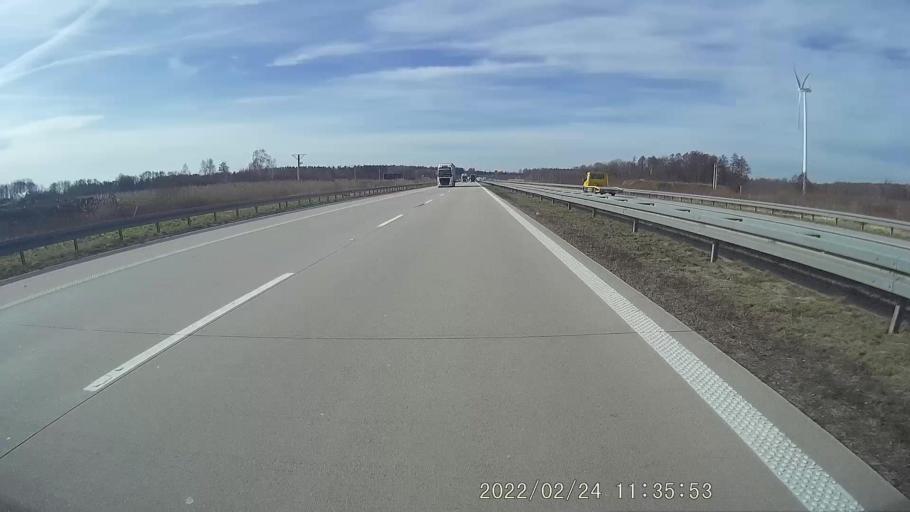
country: PL
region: Lower Silesian Voivodeship
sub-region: Powiat polkowicki
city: Przemkow
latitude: 51.5241
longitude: 15.7992
